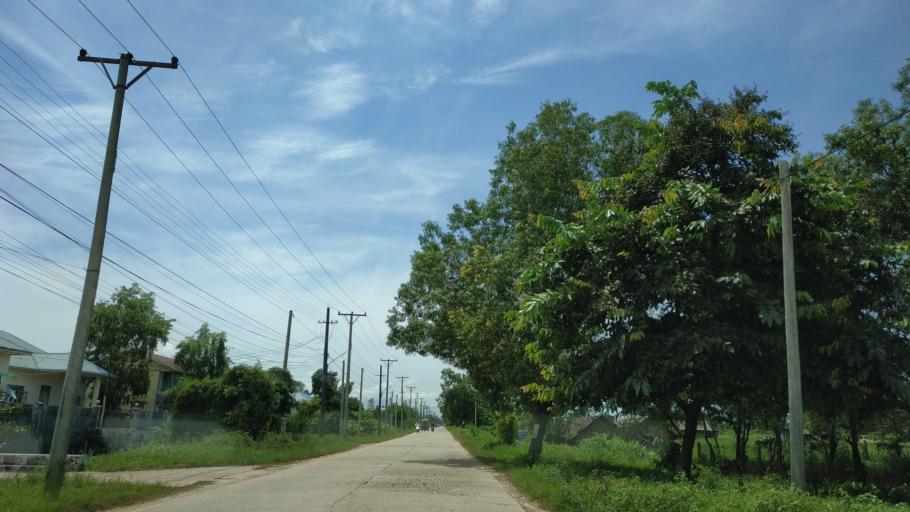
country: MM
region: Tanintharyi
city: Dawei
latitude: 14.0863
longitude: 98.1791
